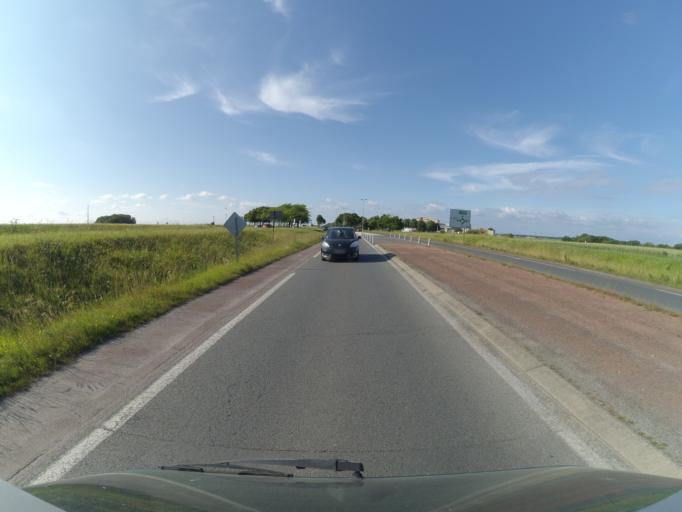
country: FR
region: Poitou-Charentes
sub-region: Departement de la Charente-Maritime
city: Saint-Sulpice-de-Royan
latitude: 45.6819
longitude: -0.9984
